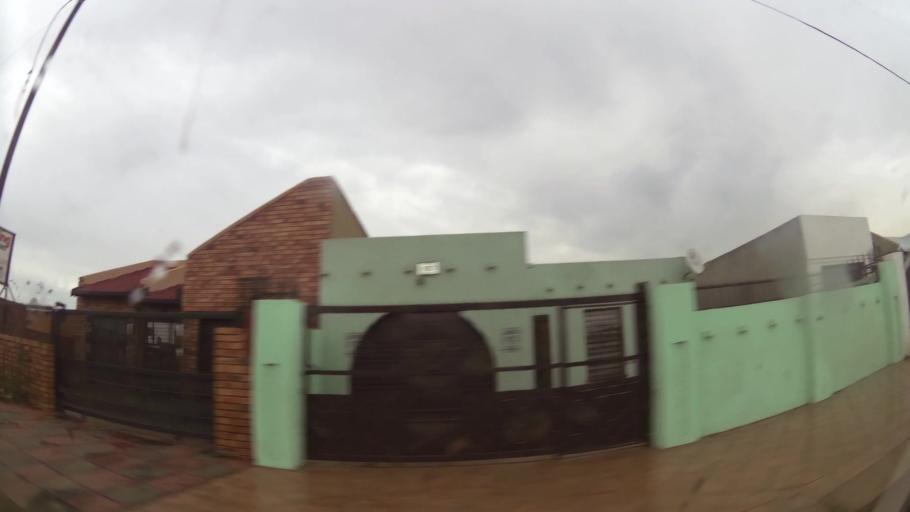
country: ZA
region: Gauteng
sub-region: Ekurhuleni Metropolitan Municipality
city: Germiston
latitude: -26.3837
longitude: 28.1799
